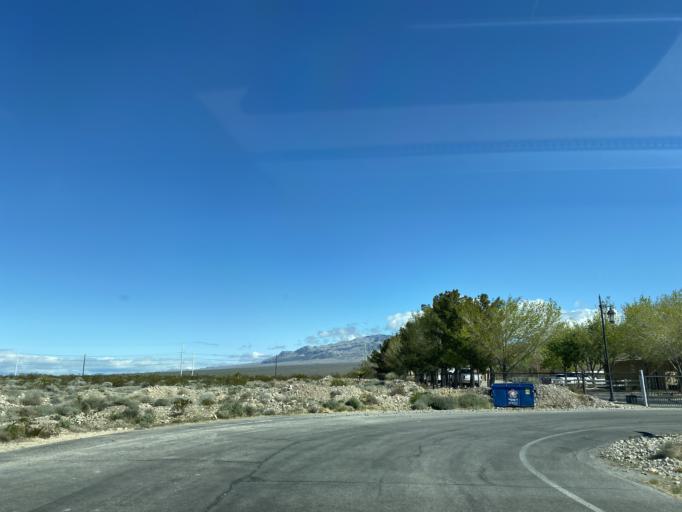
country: US
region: Nevada
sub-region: Clark County
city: North Las Vegas
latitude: 36.3303
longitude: -115.2876
